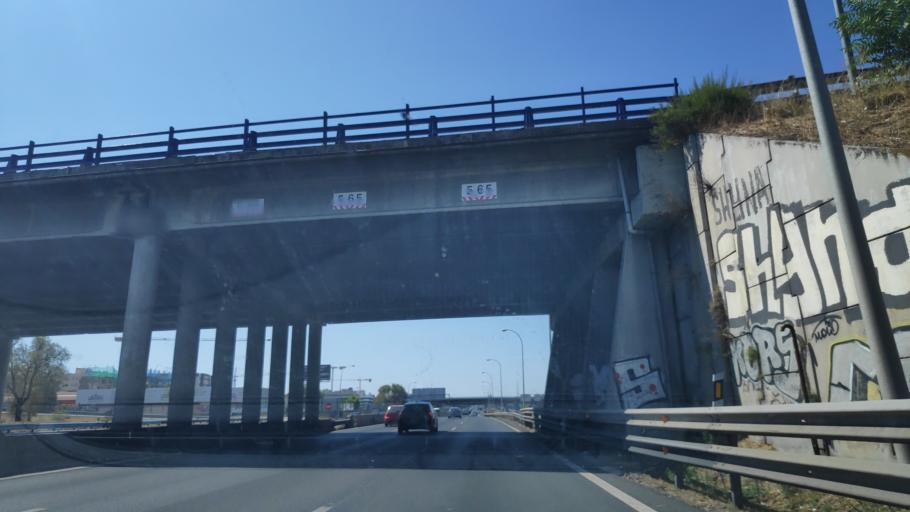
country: ES
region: Madrid
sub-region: Provincia de Madrid
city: Getafe
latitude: 40.3228
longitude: -3.7306
